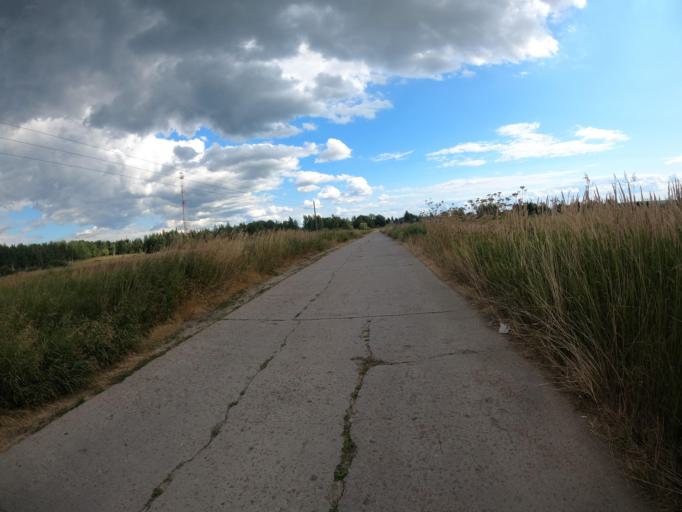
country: RU
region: Moskovskaya
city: Konobeyevo
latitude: 55.3999
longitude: 38.6737
